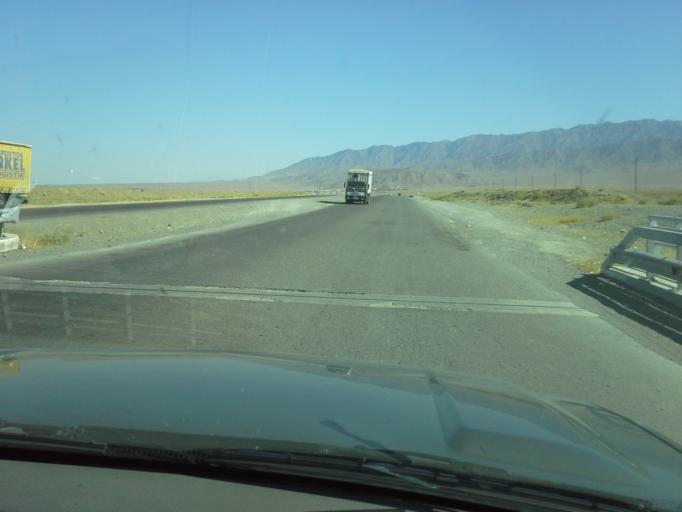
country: TM
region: Ahal
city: Baharly
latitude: 38.5659
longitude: 57.1298
